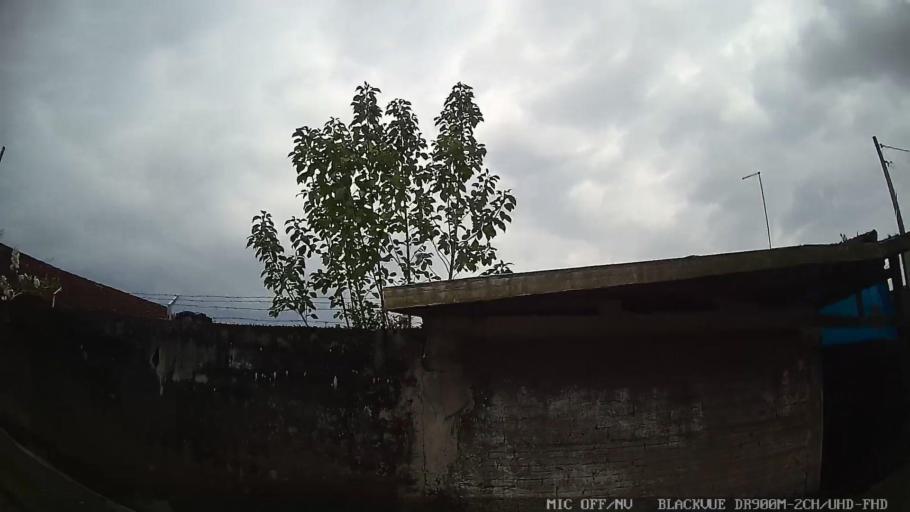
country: BR
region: Sao Paulo
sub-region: Caraguatatuba
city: Caraguatatuba
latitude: -23.6169
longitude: -45.4151
